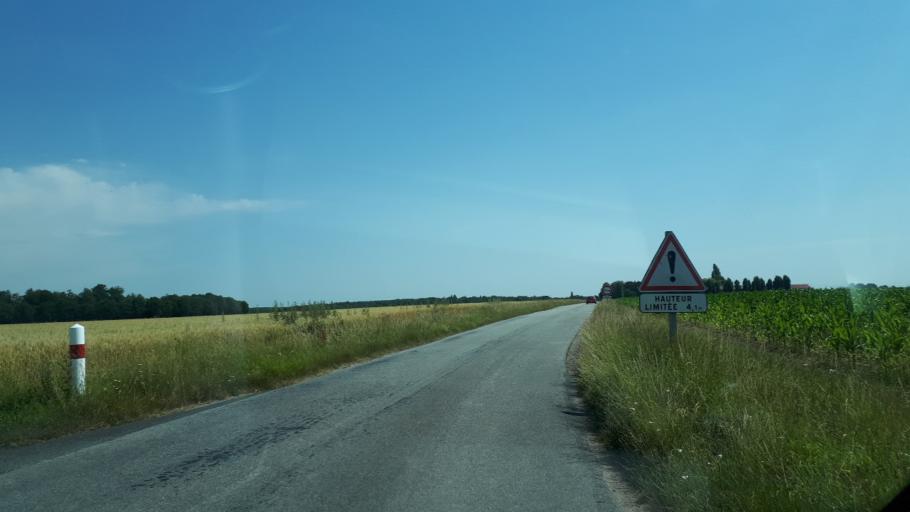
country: FR
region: Centre
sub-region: Departement d'Eure-et-Loir
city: Arrou
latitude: 48.0682
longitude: 1.1113
